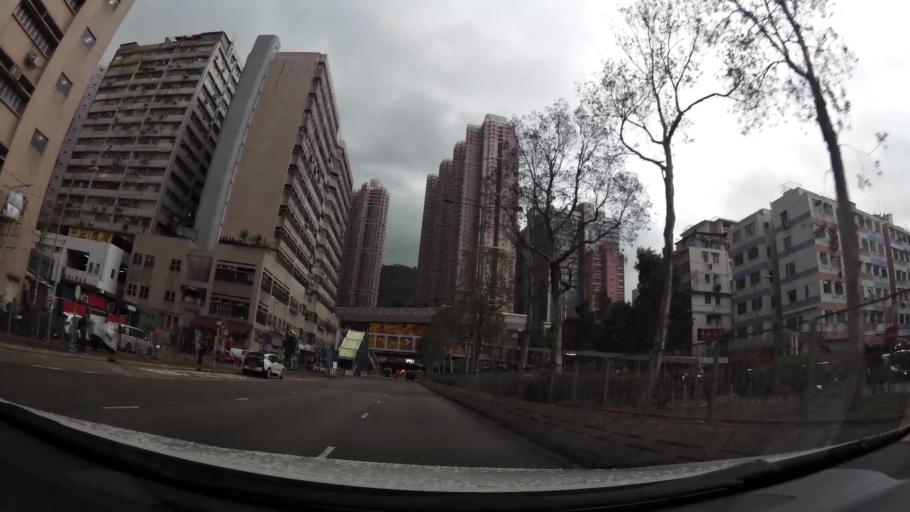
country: HK
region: Tsuen Wan
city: Tsuen Wan
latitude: 22.3737
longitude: 114.1110
